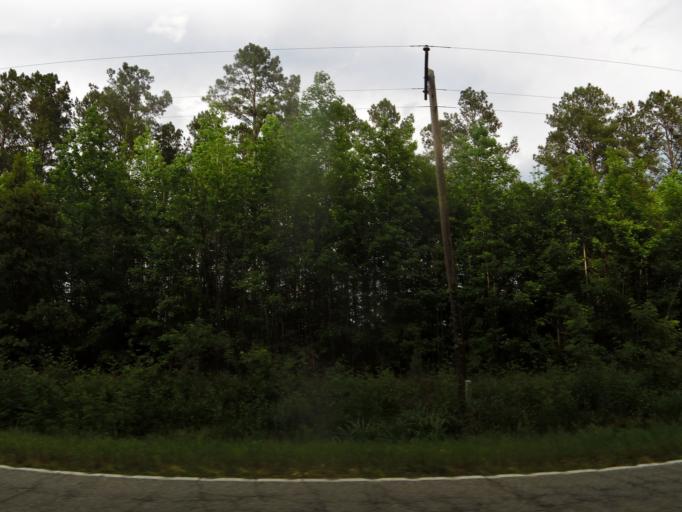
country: US
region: South Carolina
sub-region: Jasper County
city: Ridgeland
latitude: 32.4821
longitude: -81.1176
